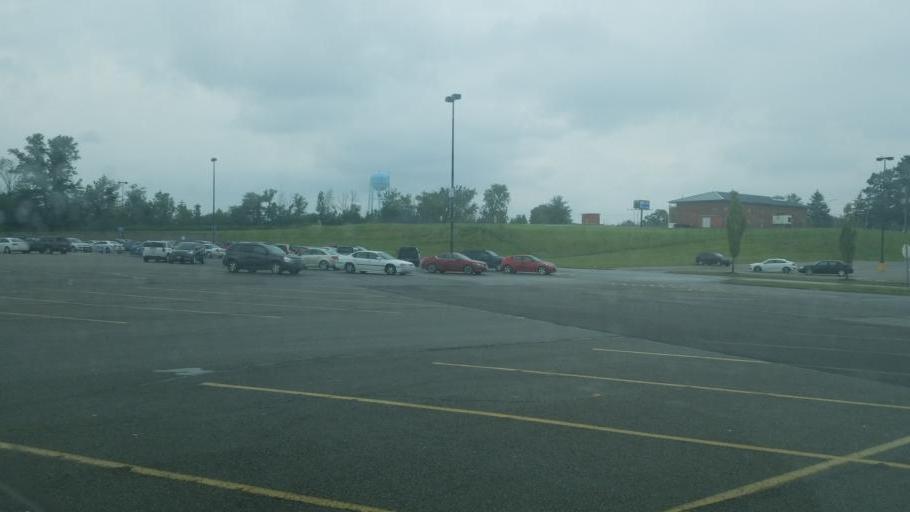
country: US
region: Ohio
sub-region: Richland County
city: Ontario
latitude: 40.7622
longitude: -82.5930
